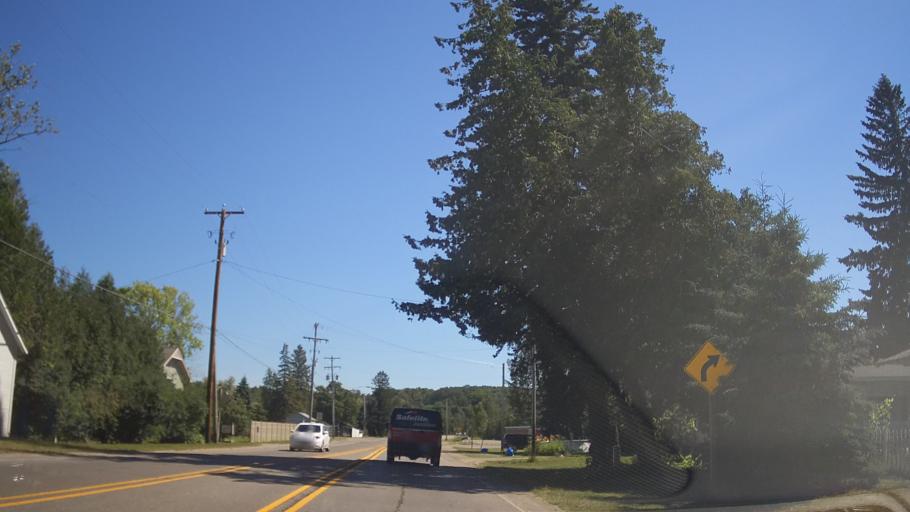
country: US
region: Michigan
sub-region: Emmet County
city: Petoskey
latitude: 45.4162
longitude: -84.8654
